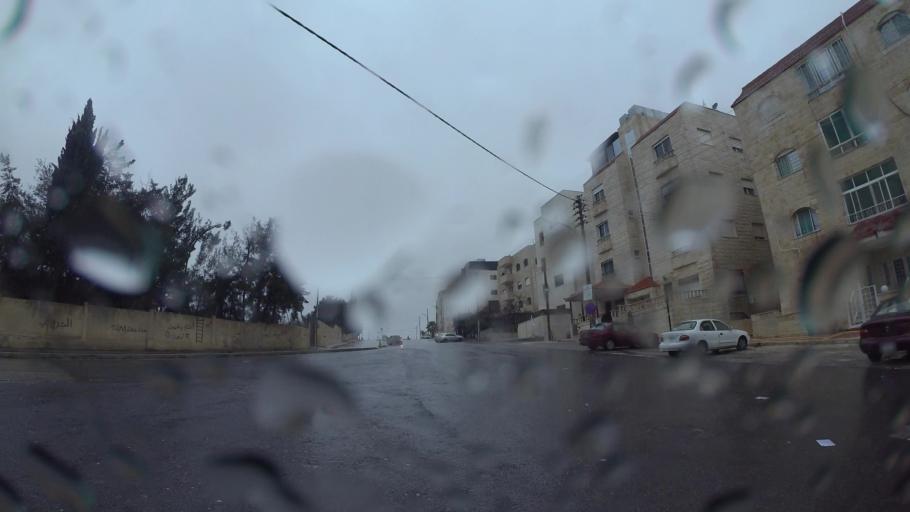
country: JO
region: Amman
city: Al Jubayhah
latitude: 32.0467
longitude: 35.8750
